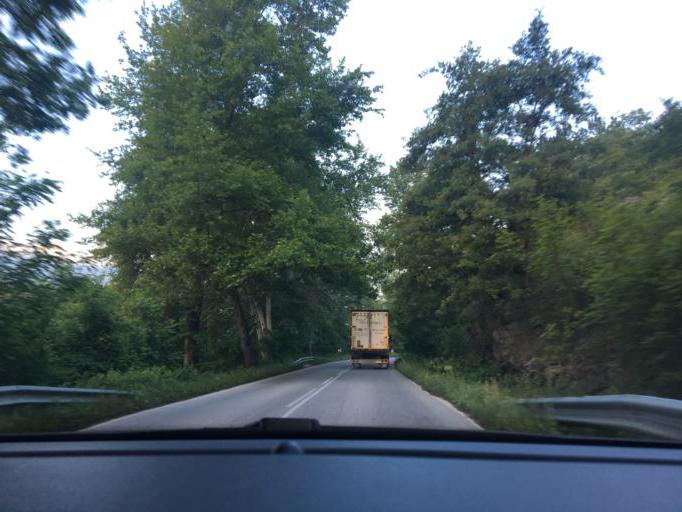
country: BG
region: Blagoevgrad
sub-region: Obshtina Petrich
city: Petrich
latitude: 41.4006
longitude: 23.0797
